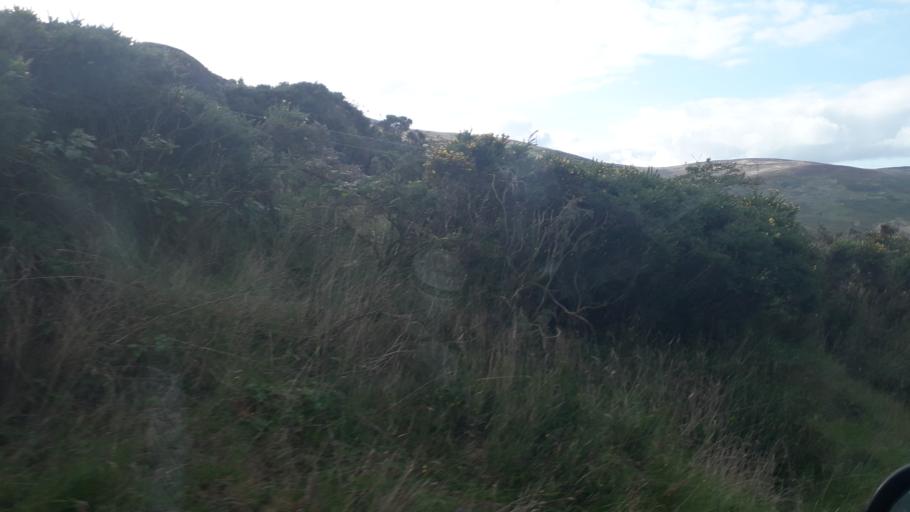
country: GB
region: Northern Ireland
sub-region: Down District
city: Warrenpoint
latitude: 54.0649
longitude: -6.2749
